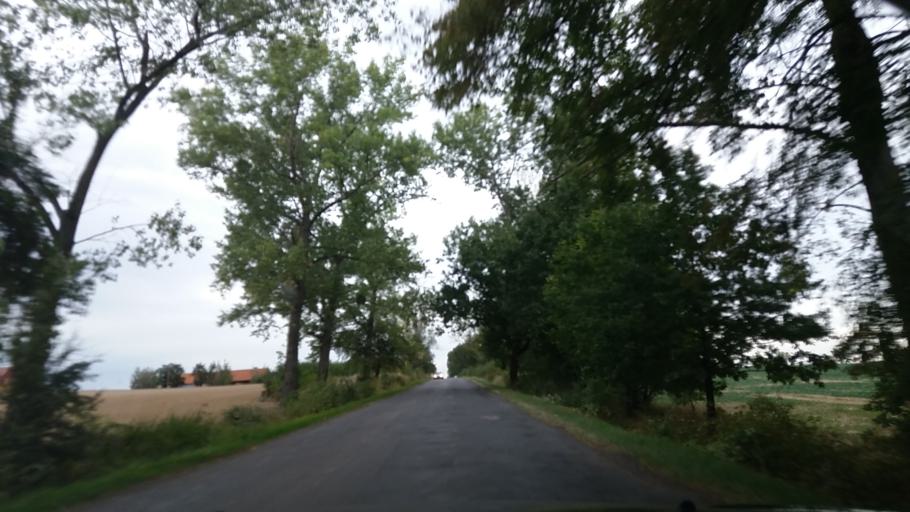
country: PL
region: Lower Silesian Voivodeship
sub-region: Powiat legnicki
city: Legnickie Pole
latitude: 51.1348
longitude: 16.3430
